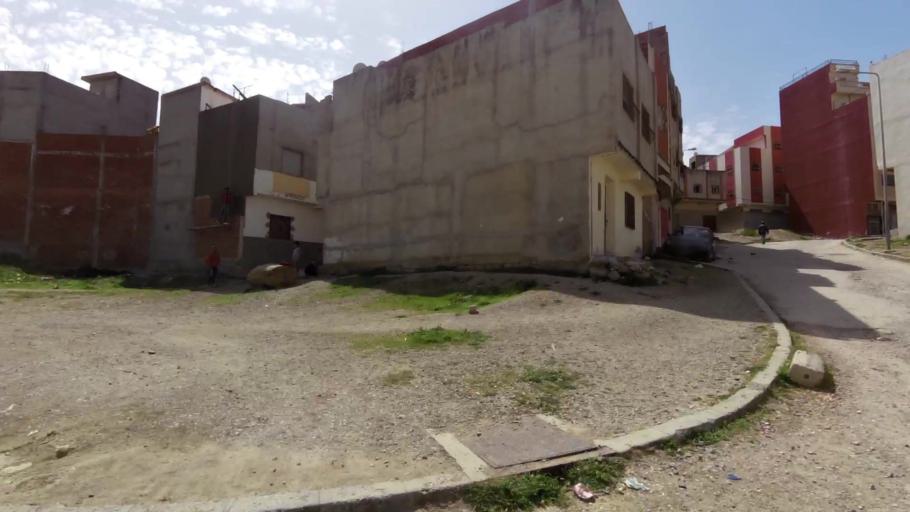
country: MA
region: Tanger-Tetouan
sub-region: Tanger-Assilah
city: Tangier
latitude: 35.7320
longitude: -5.8110
